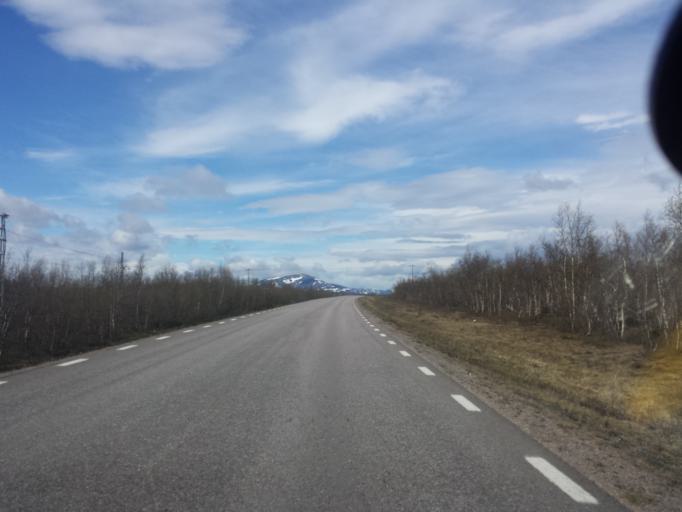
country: SE
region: Norrbotten
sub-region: Kiruna Kommun
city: Kiruna
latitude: 68.0596
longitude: 19.8257
